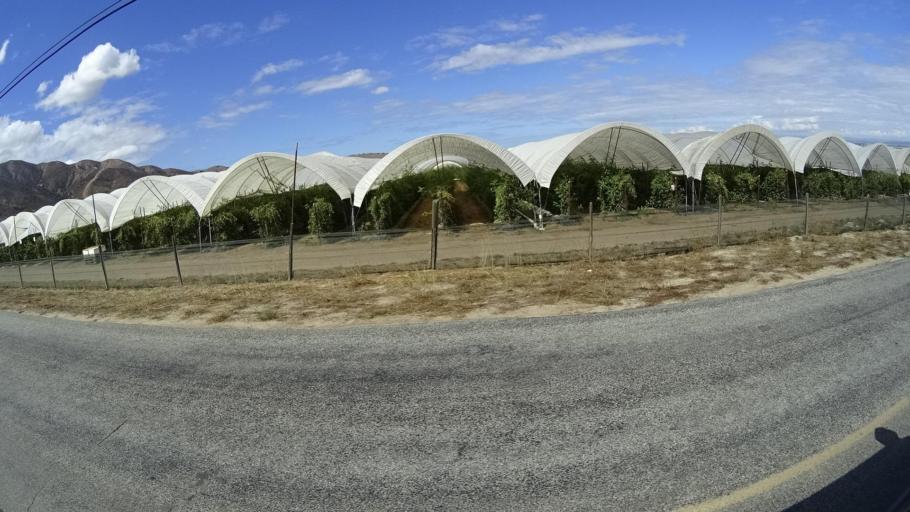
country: US
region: California
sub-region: Monterey County
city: Salinas
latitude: 36.5914
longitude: -121.6253
